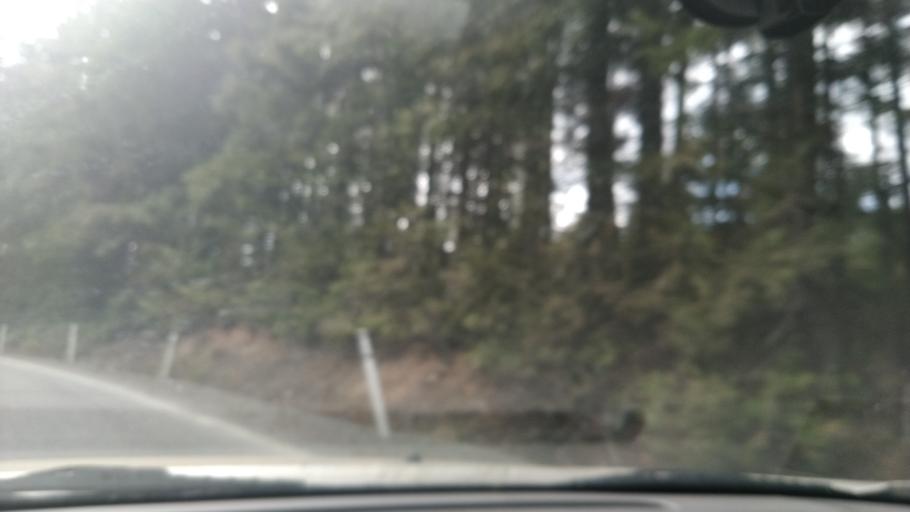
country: CA
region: British Columbia
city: Campbell River
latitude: 49.9862
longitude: -125.4118
